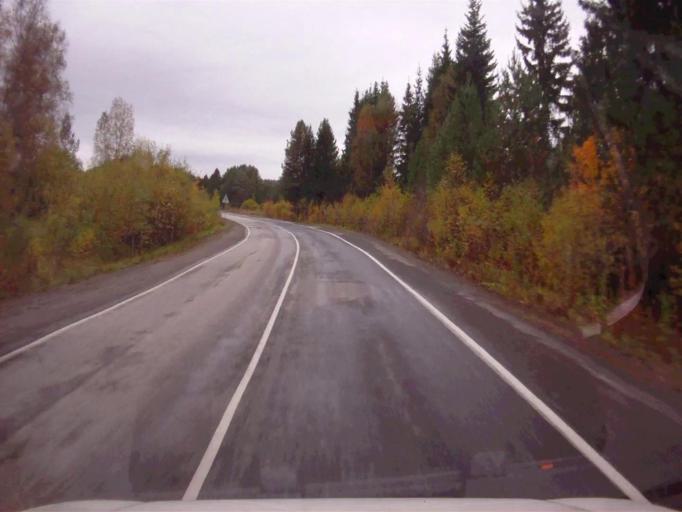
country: RU
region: Chelyabinsk
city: Nyazepetrovsk
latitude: 56.0668
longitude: 59.6983
